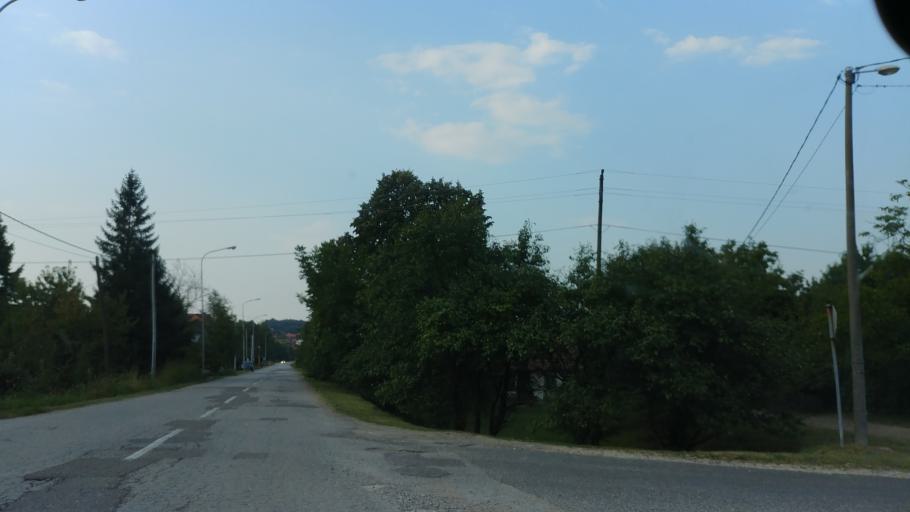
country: BA
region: Republika Srpska
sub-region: Opstina Ugljevik
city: Ugljevik
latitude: 44.6910
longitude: 19.0137
